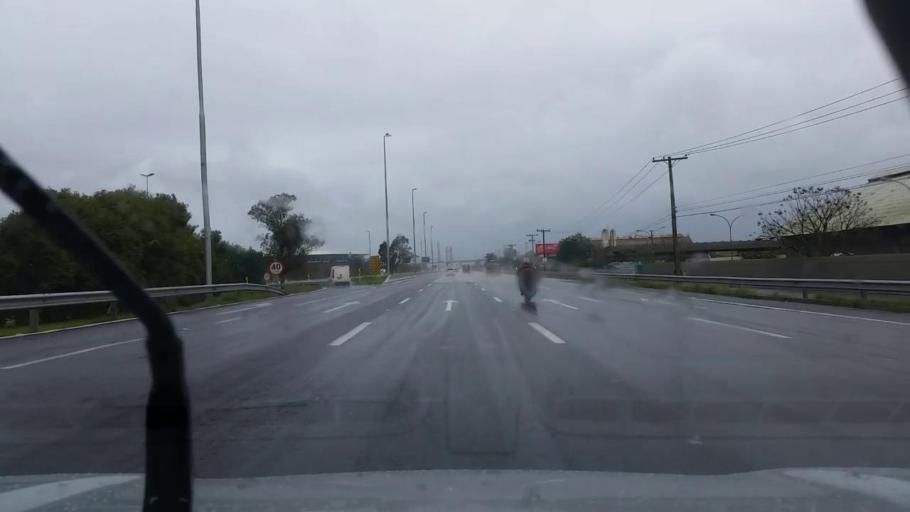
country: BR
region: Rio Grande do Sul
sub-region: Canoas
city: Canoas
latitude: -29.9700
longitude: -51.1813
